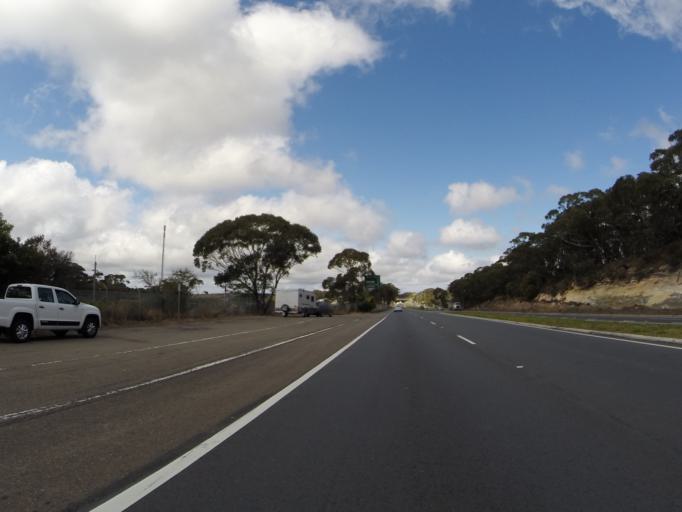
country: AU
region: New South Wales
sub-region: Sutherland Shire
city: Heathcote
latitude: -34.1289
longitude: 150.9934
